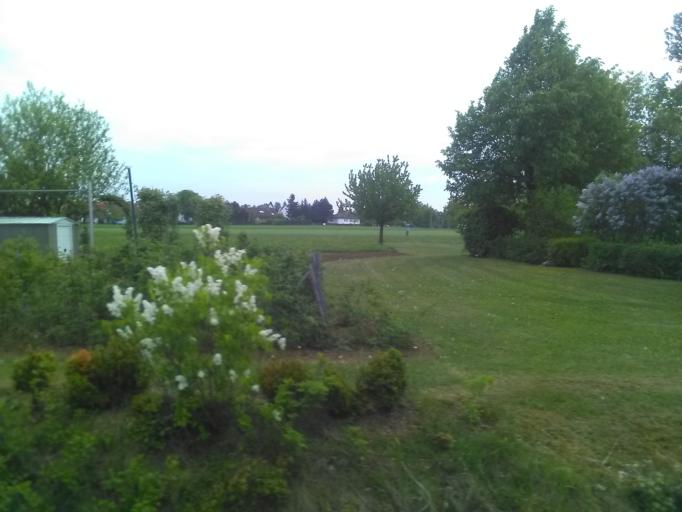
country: DE
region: Bavaria
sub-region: Regierungsbezirk Mittelfranken
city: Kalchreuth
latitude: 49.5601
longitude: 11.1418
